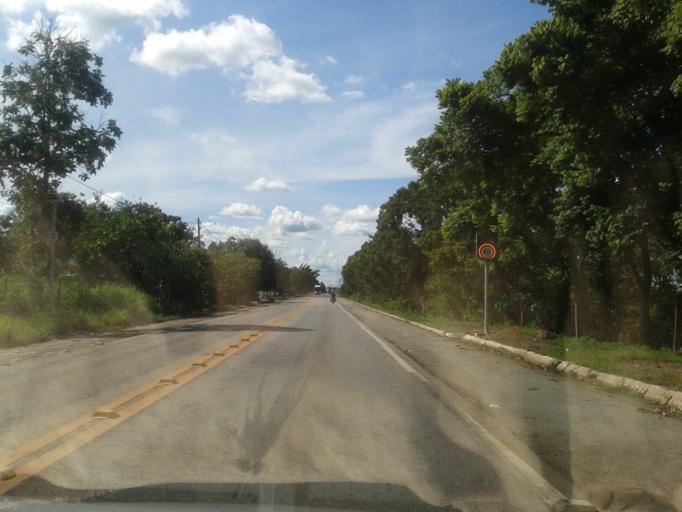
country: BR
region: Goias
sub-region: Mozarlandia
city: Mozarlandia
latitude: -15.2499
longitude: -50.5027
